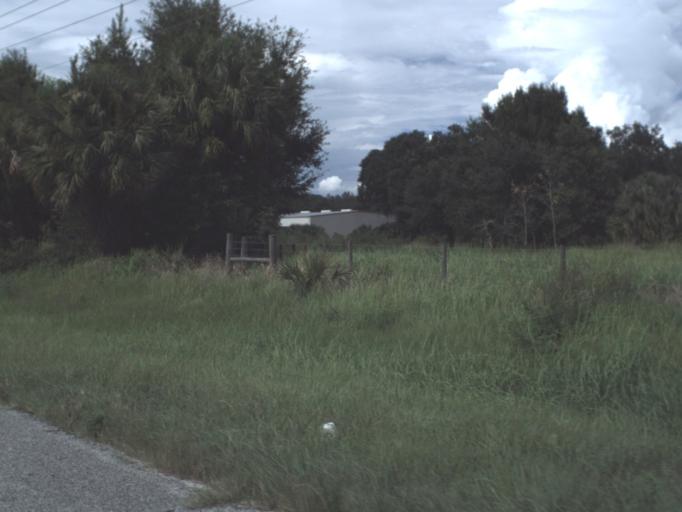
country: US
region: Florida
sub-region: Polk County
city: Willow Oak
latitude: 27.9208
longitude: -82.0271
